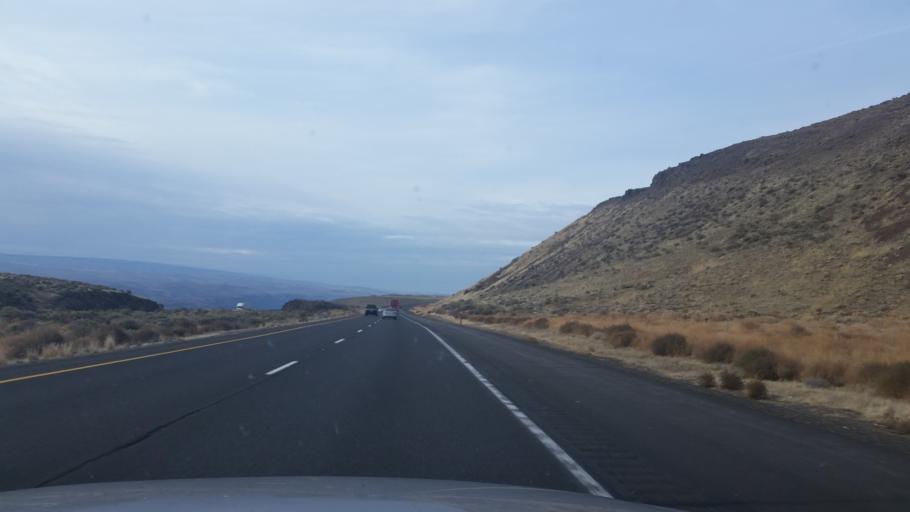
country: US
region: Washington
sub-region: Grant County
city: Mattawa
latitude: 46.9935
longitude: -119.9707
